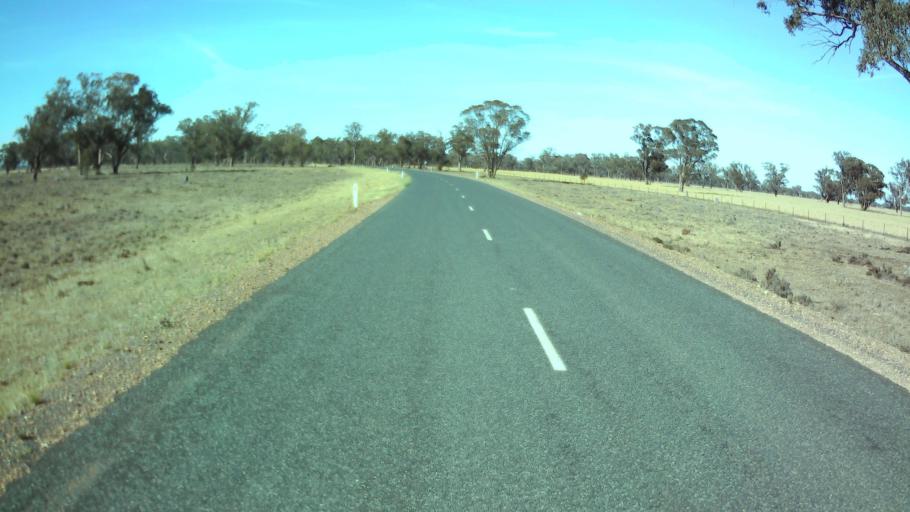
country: AU
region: New South Wales
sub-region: Weddin
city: Grenfell
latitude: -34.0581
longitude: 147.9123
